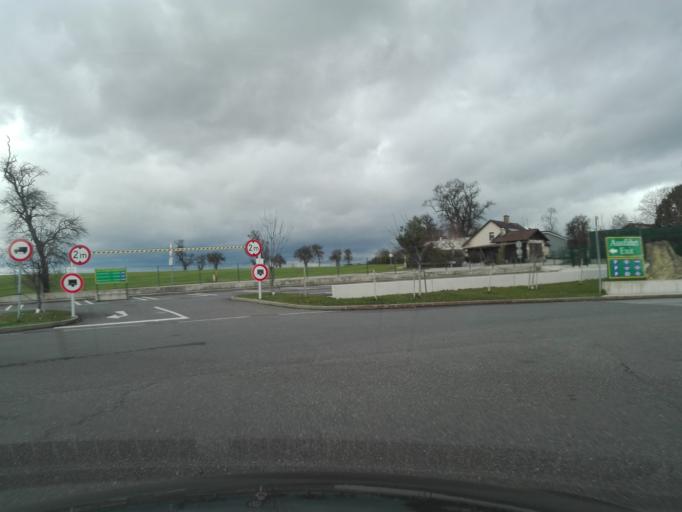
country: AT
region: Lower Austria
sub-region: Politischer Bezirk Amstetten
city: Zeillern
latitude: 48.1181
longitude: 14.7329
